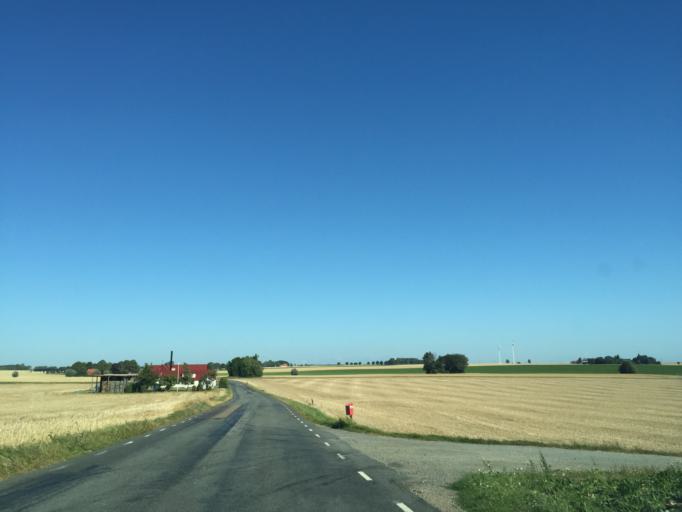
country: SE
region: Skane
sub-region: Ystads Kommun
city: Kopingebro
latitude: 55.4471
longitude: 14.1208
